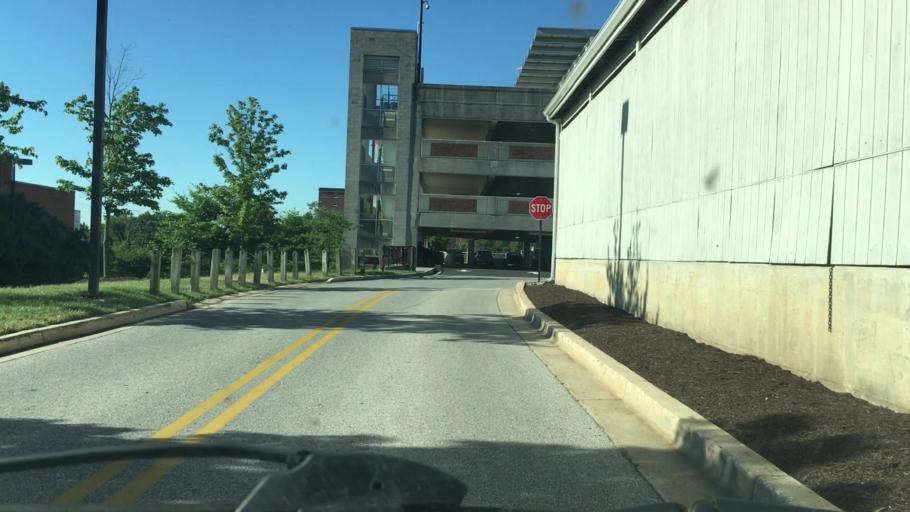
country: US
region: Maryland
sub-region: Prince George's County
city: College Park
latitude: 38.9957
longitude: -76.9426
